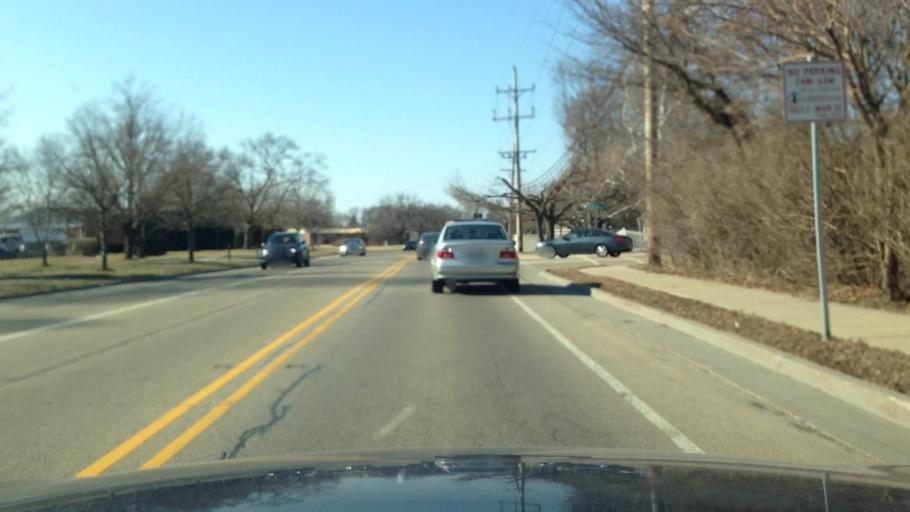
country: US
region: Illinois
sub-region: Cook County
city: Glenview
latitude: 42.0557
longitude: -87.8123
